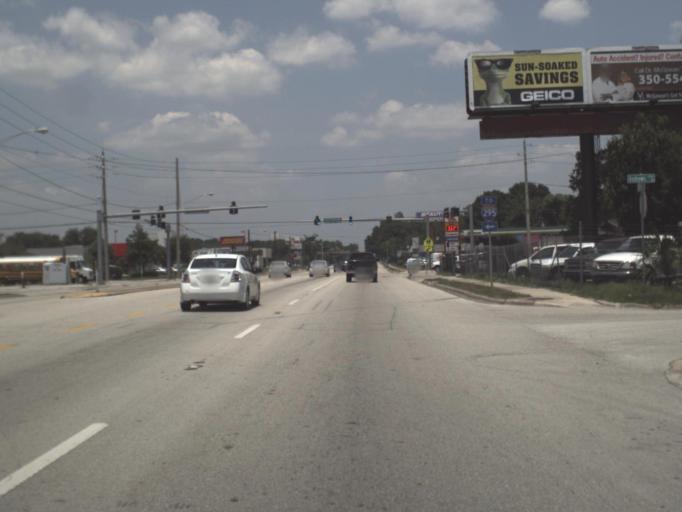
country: US
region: Florida
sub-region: Duval County
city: Jacksonville
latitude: 30.3355
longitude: -81.7310
